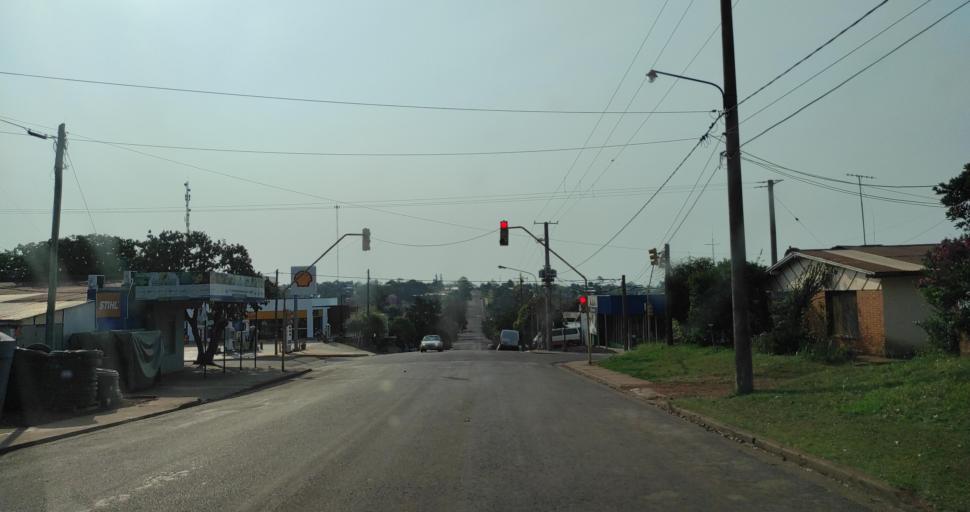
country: AR
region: Misiones
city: Cerro Azul
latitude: -27.6346
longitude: -55.4936
